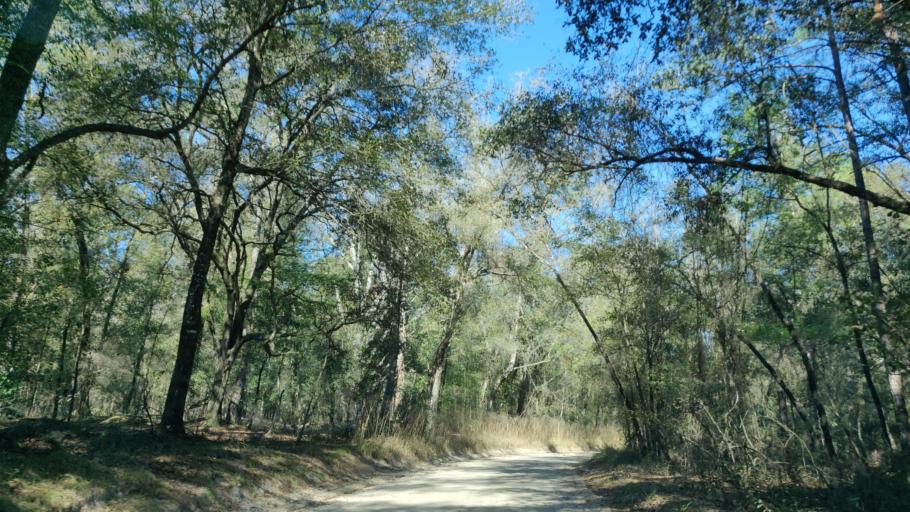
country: US
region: Florida
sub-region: Clay County
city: Middleburg
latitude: 30.1546
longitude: -81.9337
